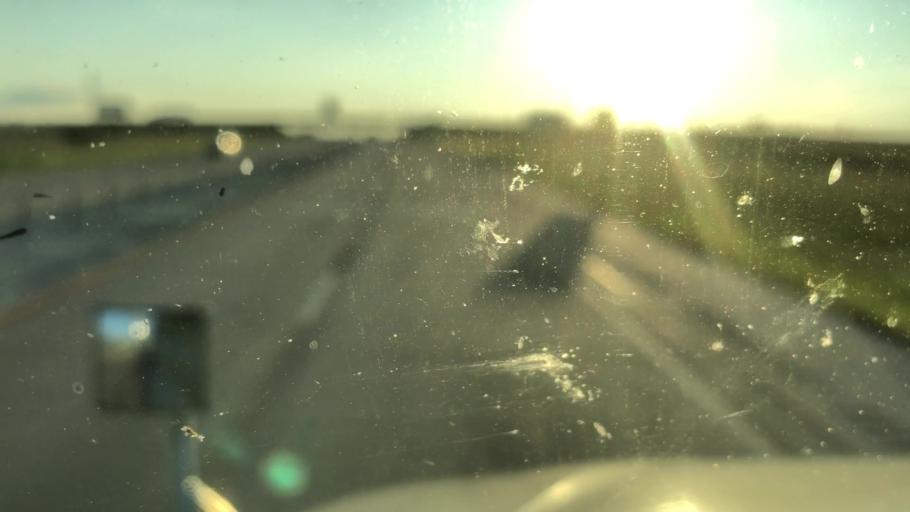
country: US
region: Oklahoma
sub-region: Noble County
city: Perry
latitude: 36.3836
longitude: -97.0627
